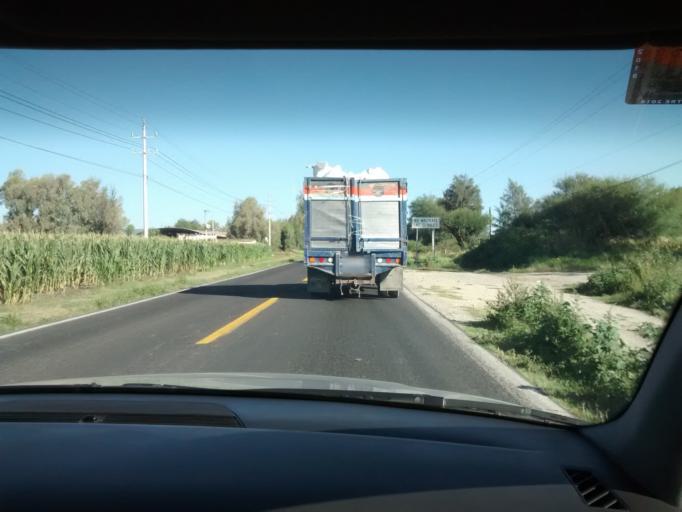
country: MX
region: Puebla
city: San Bartolo Teontepec
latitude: 18.5366
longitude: -97.5307
